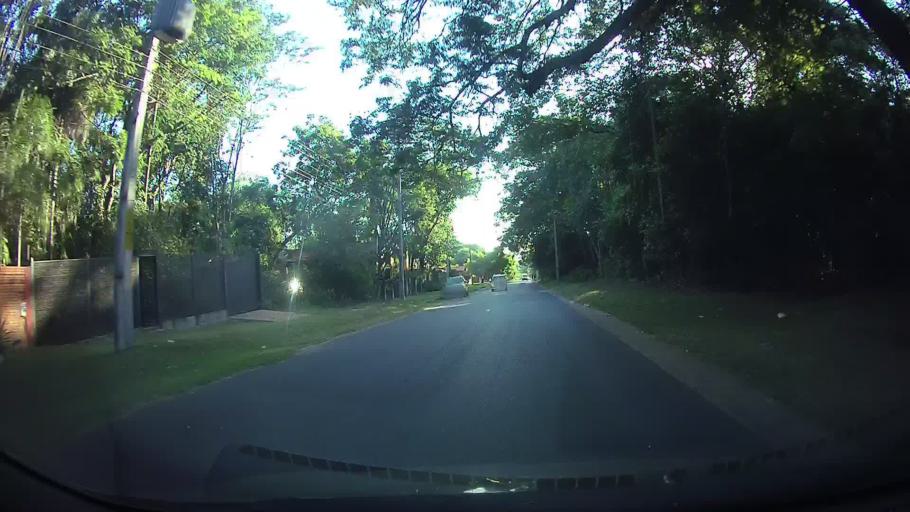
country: PY
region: Cordillera
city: San Bernardino
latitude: -25.3197
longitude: -57.2718
